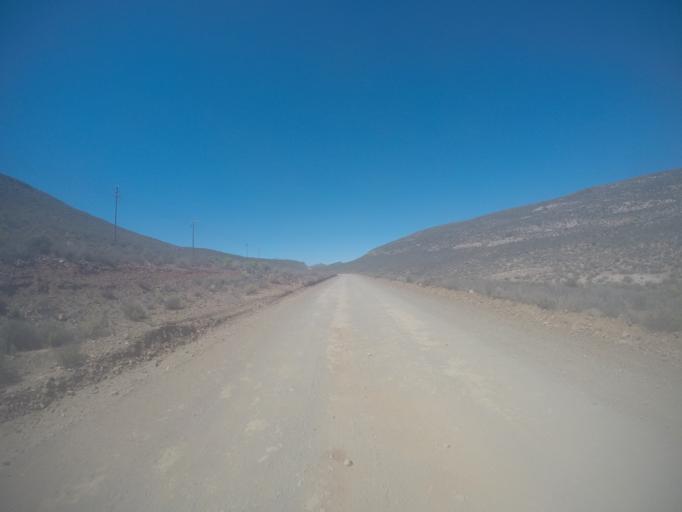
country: ZA
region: Western Cape
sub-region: West Coast District Municipality
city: Clanwilliam
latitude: -32.5226
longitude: 19.3509
